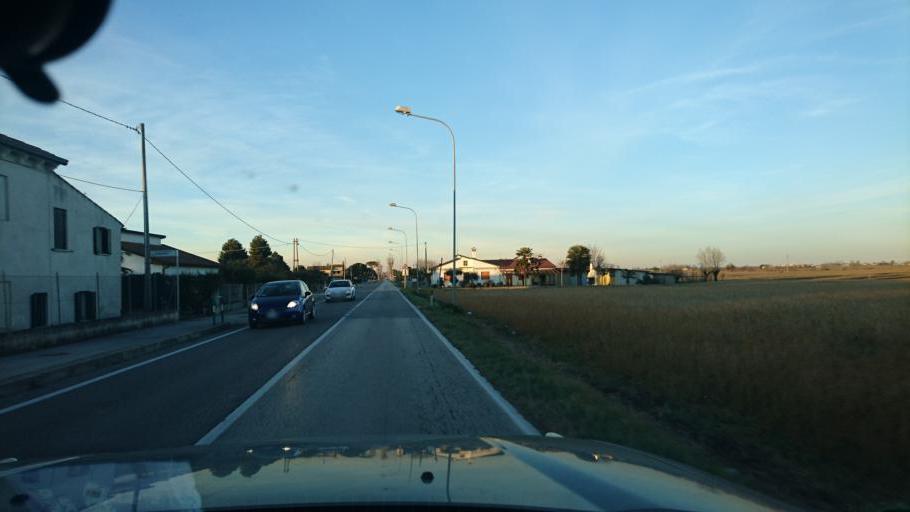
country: IT
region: Veneto
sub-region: Provincia di Venezia
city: Pegolotte
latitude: 45.1979
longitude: 12.0390
